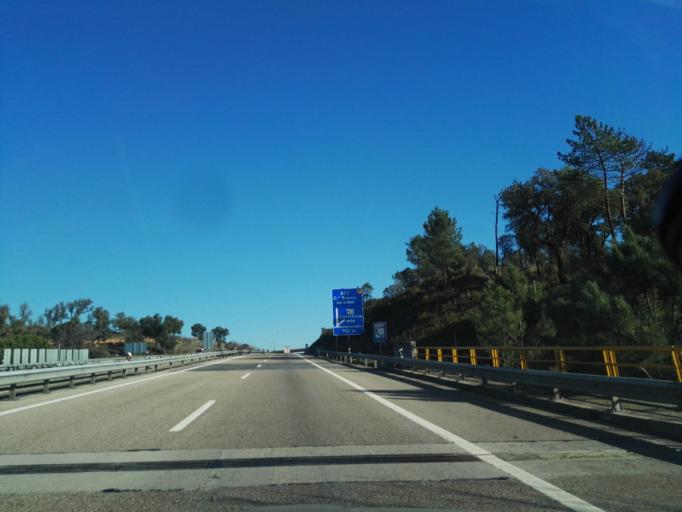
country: PT
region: Santarem
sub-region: Constancia
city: Constancia
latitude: 39.4828
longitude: -8.3397
